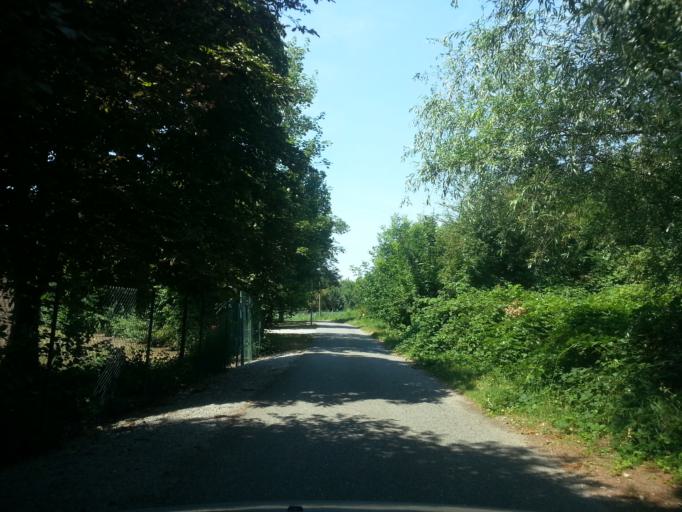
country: DE
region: Hesse
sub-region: Regierungsbezirk Darmstadt
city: Burstadt
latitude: 49.6358
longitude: 8.4551
